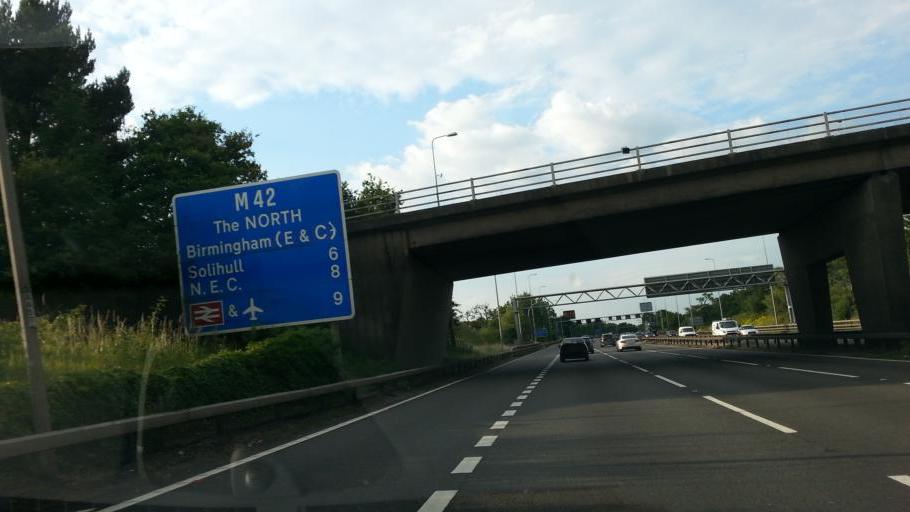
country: GB
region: England
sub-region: Solihull
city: Cheswick Green
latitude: 52.3558
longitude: -1.8085
